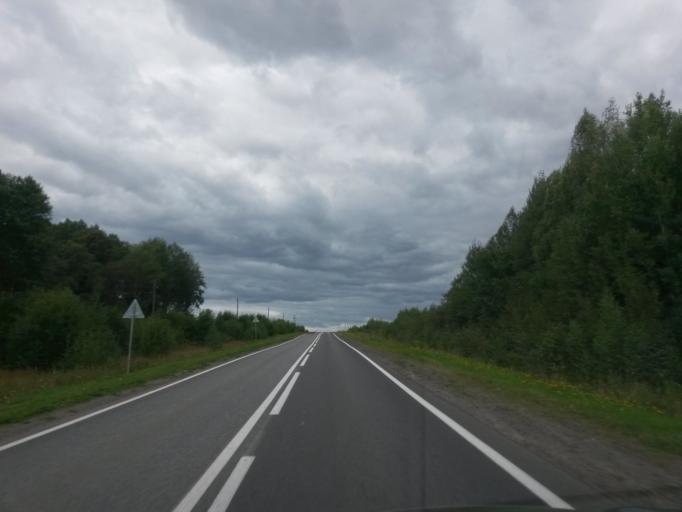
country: RU
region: Jaroslavl
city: Konstantinovskiy
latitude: 57.8169
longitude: 39.7110
